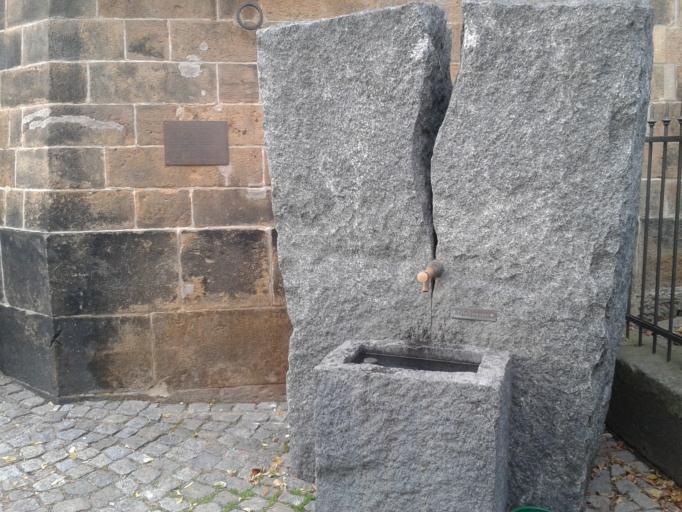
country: DE
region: Saxony
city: Stadt Wehlen
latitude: 50.9572
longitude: 14.0338
